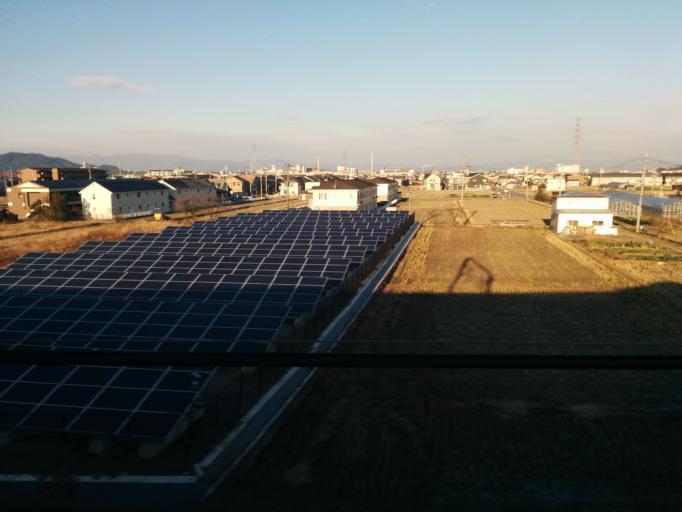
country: JP
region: Shiga Prefecture
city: Hikone
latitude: 35.2389
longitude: 136.2664
